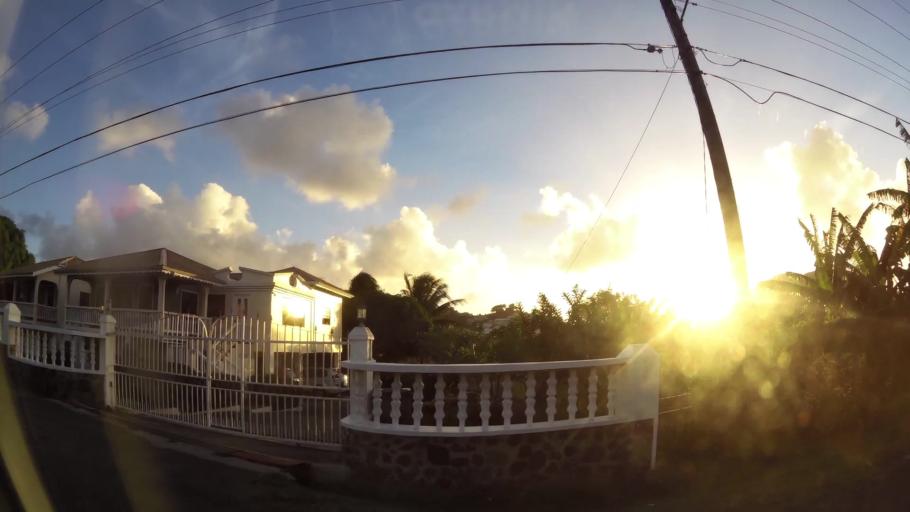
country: LC
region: Gros-Islet
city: Gros Islet
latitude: 14.0717
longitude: -60.9455
